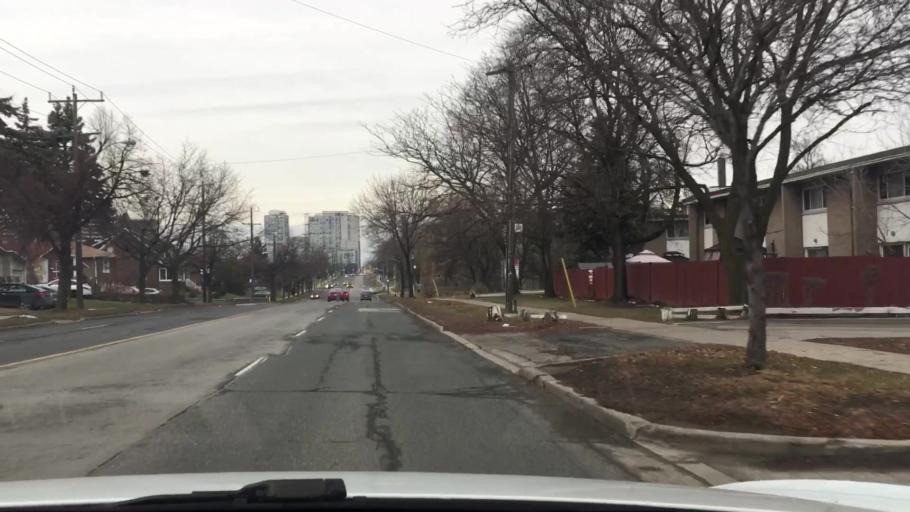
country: CA
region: Ontario
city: Scarborough
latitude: 43.7441
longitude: -79.2620
